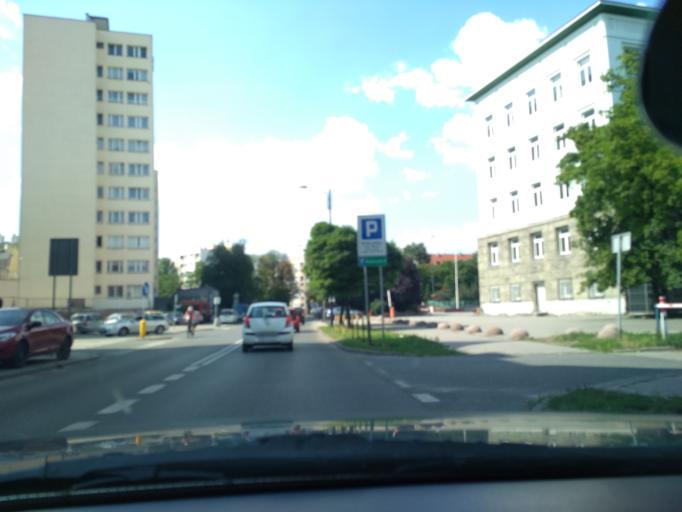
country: PL
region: Silesian Voivodeship
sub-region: Gliwice
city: Gliwice
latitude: 50.2904
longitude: 18.6730
